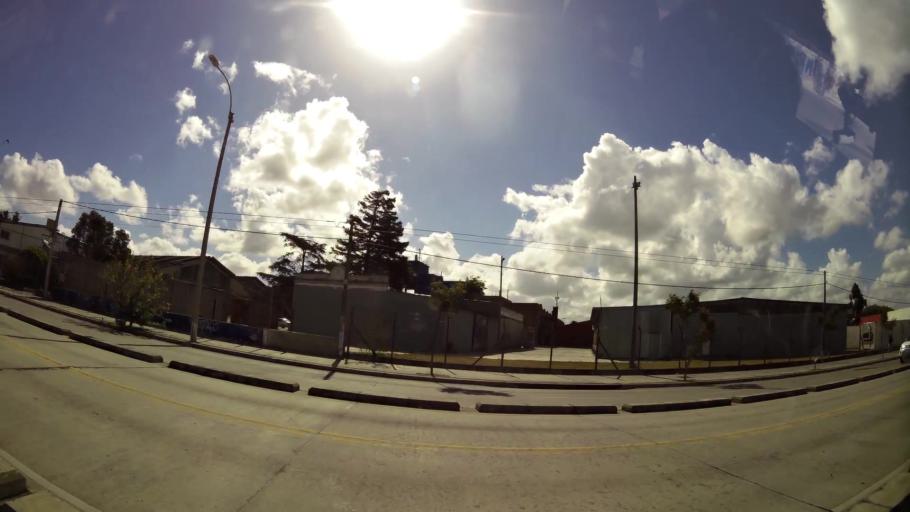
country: UY
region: Canelones
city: La Paz
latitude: -34.8286
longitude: -56.2202
